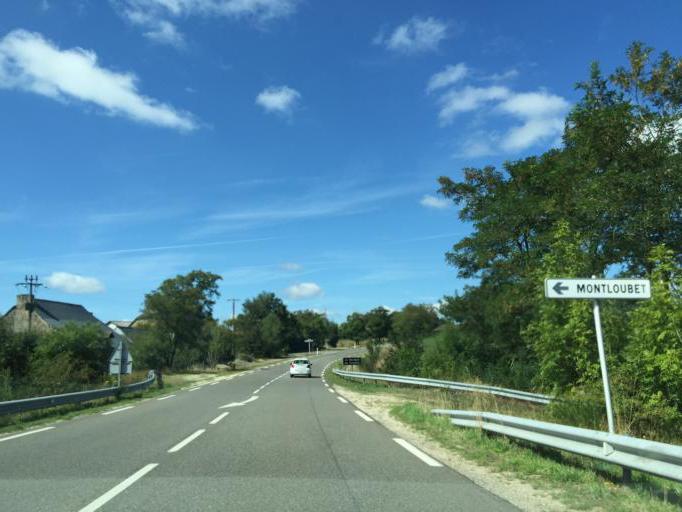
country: FR
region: Midi-Pyrenees
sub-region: Departement de l'Aveyron
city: Rieupeyroux
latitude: 44.3069
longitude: 2.1613
